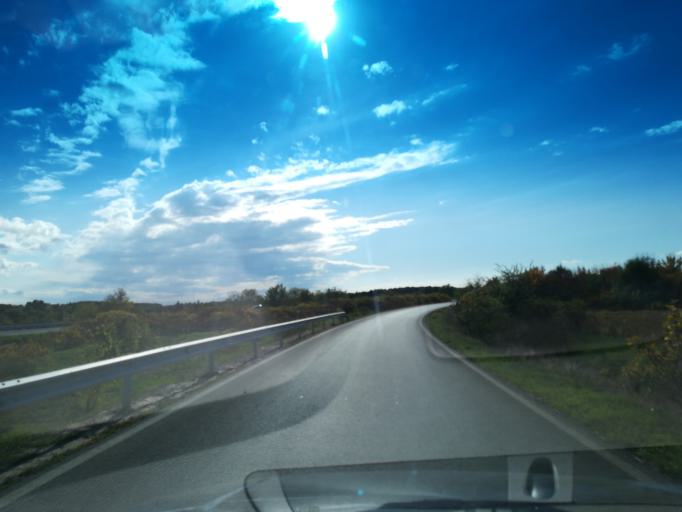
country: BG
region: Stara Zagora
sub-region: Obshtina Stara Zagora
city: Stara Zagora
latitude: 42.3397
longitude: 25.6597
